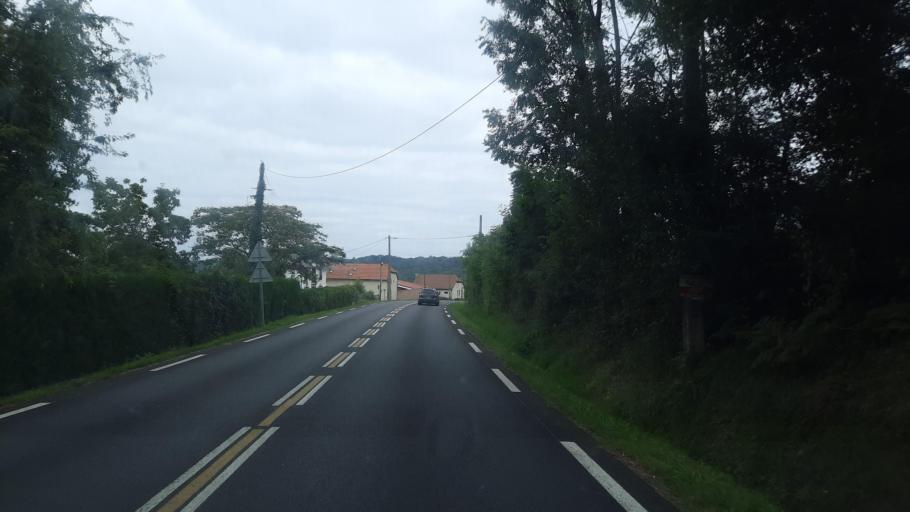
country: FR
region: Midi-Pyrenees
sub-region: Departement des Hautes-Pyrenees
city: Semeac
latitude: 43.2415
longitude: 0.1186
